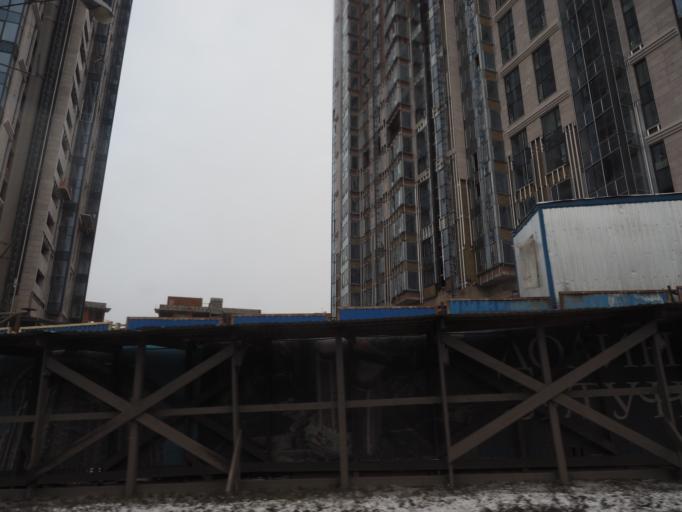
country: RU
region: Moskovskaya
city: Kastanayevo
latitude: 55.7158
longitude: 37.5032
